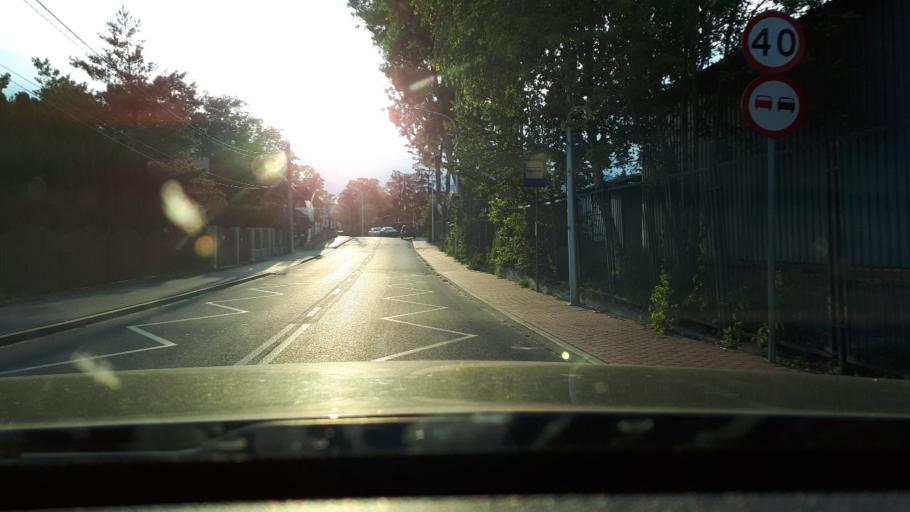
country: PL
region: Masovian Voivodeship
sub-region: Powiat pruszkowski
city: Komorow
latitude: 52.1546
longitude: 20.8094
